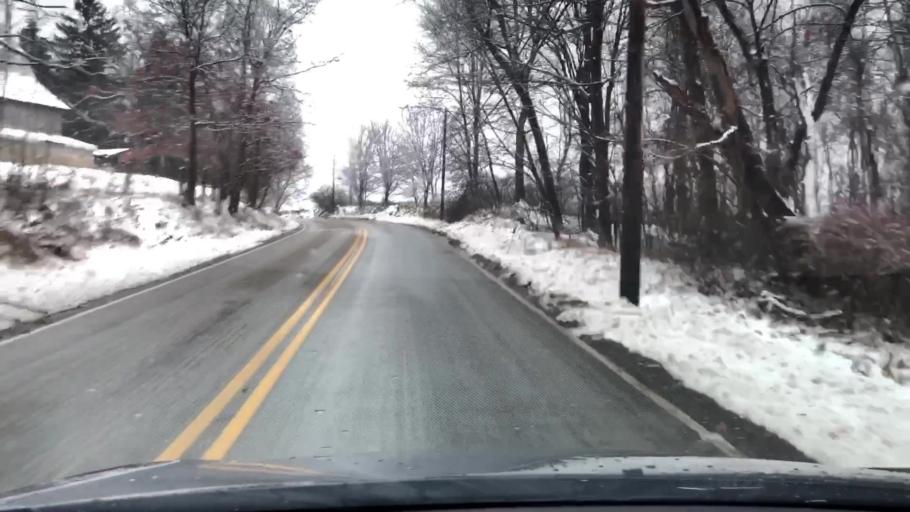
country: US
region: Pennsylvania
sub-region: Fayette County
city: Dunbar
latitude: 39.8289
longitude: -79.5355
